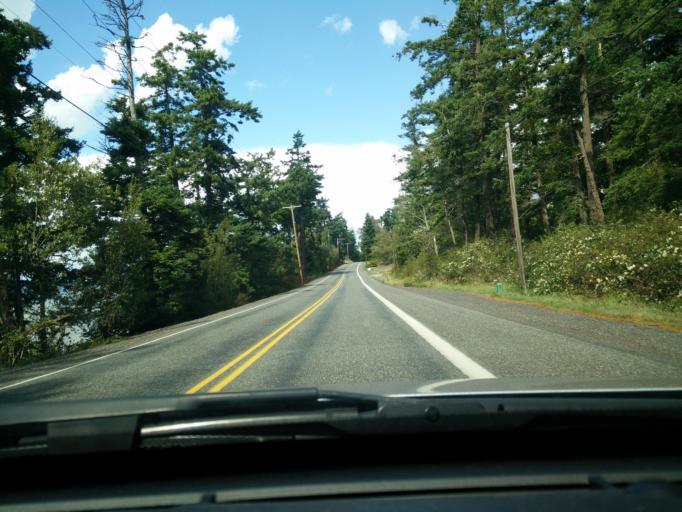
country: US
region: Washington
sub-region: Skagit County
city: Anacortes
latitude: 48.4892
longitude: -122.4811
